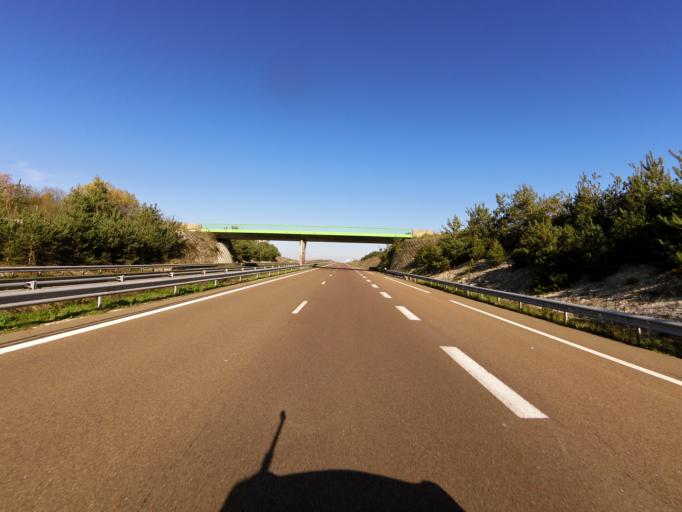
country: FR
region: Champagne-Ardenne
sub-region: Departement de la Marne
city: Compertrix
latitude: 48.8900
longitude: 4.2889
